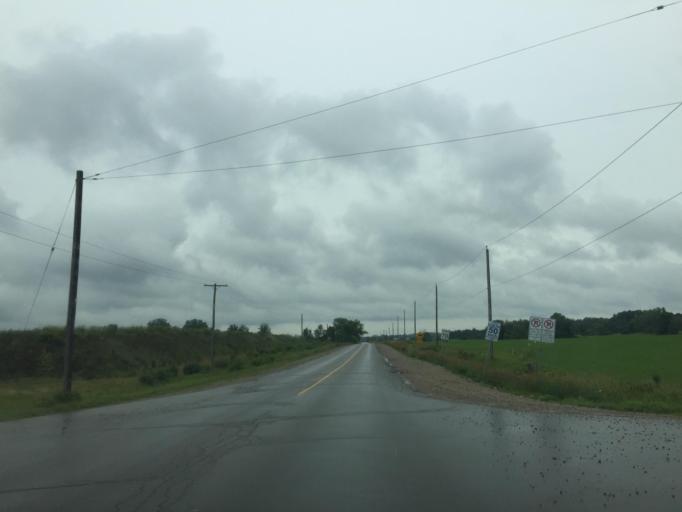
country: CA
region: Ontario
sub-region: Wellington County
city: Guelph
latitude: 43.4781
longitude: -80.2268
